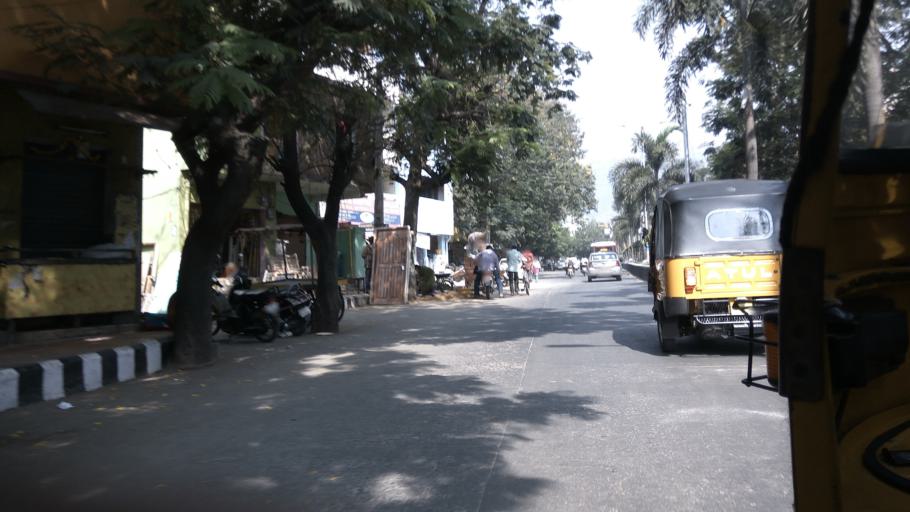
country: IN
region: Andhra Pradesh
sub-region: Chittoor
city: Tirupati
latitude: 13.6368
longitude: 79.4117
